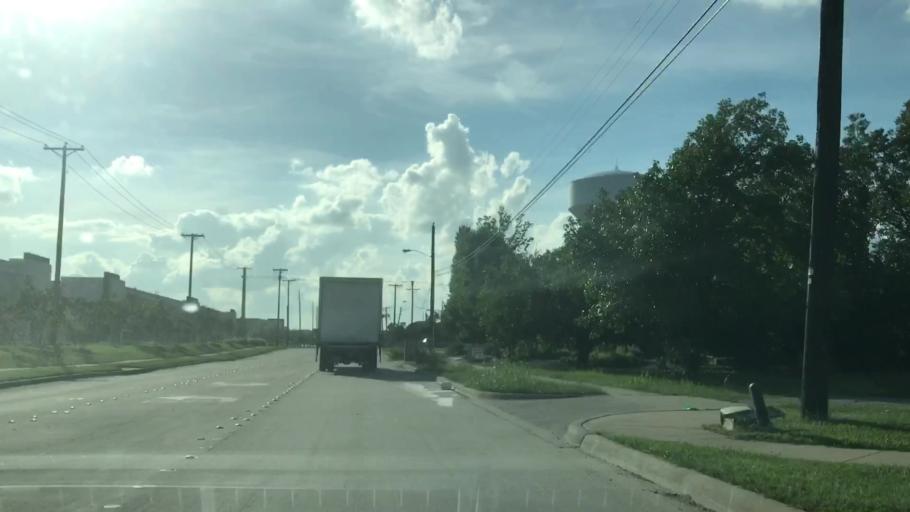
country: US
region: Texas
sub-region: Dallas County
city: Coppell
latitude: 32.9489
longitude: -97.0037
